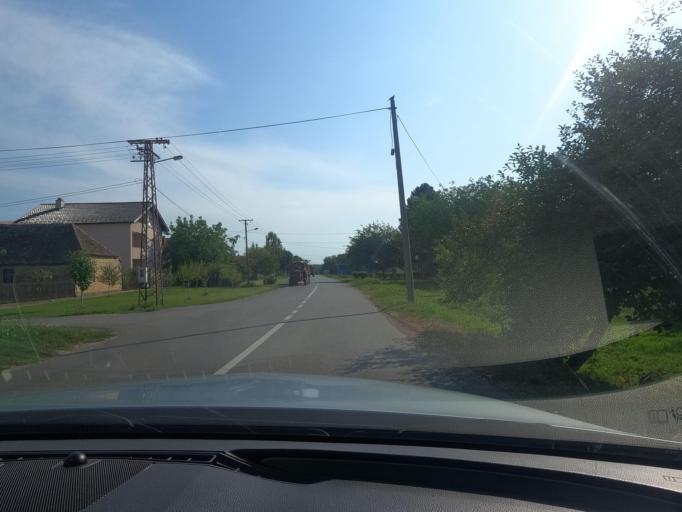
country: RS
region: Autonomna Pokrajina Vojvodina
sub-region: Juznobacki Okrug
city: Kovilj
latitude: 45.2226
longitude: 20.0375
